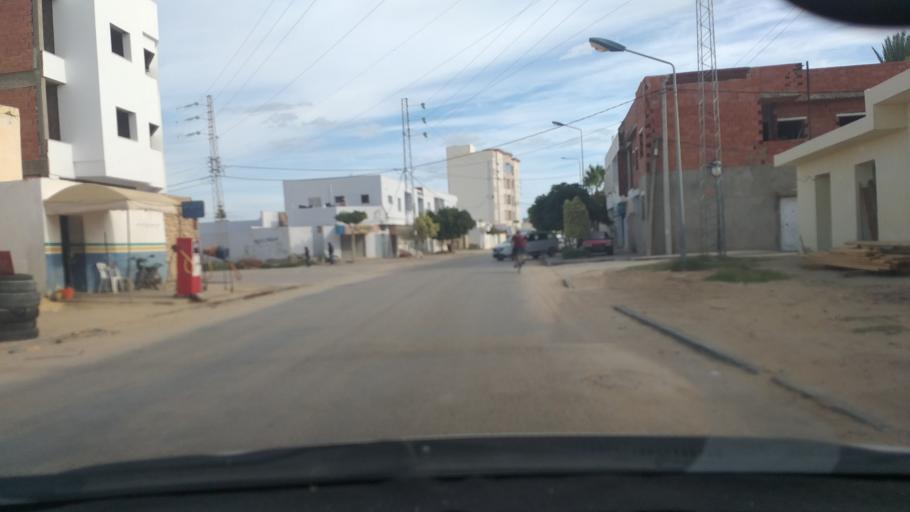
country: TN
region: Safaqis
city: Al Qarmadah
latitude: 34.7980
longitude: 10.7983
